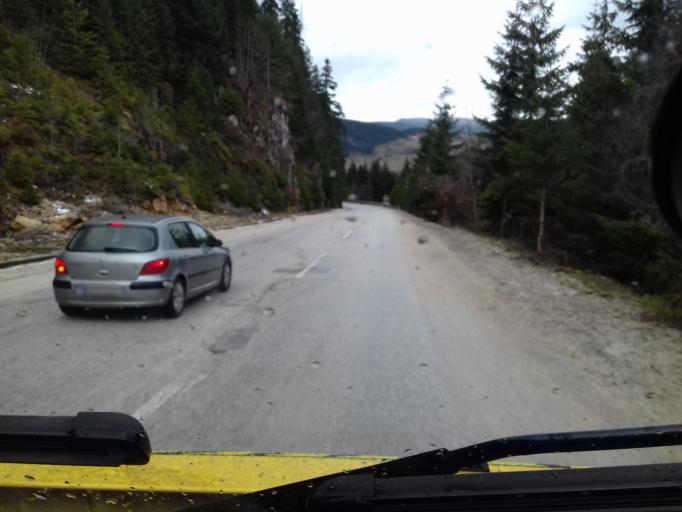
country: BA
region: Federation of Bosnia and Herzegovina
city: Turbe
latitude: 44.3164
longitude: 17.5135
